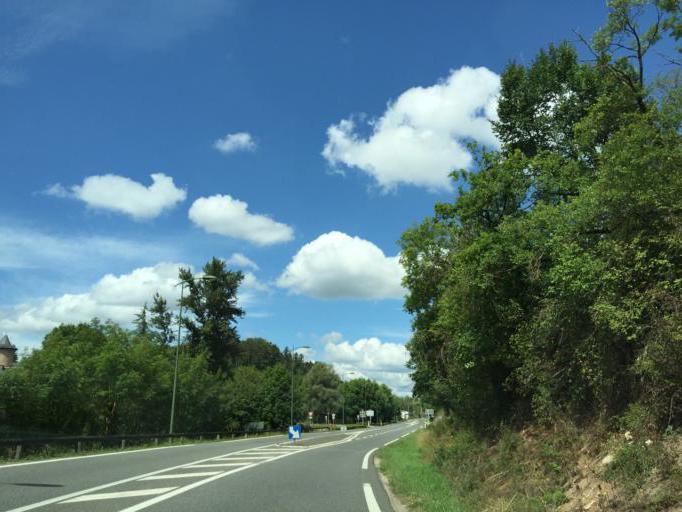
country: FR
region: Midi-Pyrenees
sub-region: Departement de l'Aveyron
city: Rodez
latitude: 44.3764
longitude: 2.5652
